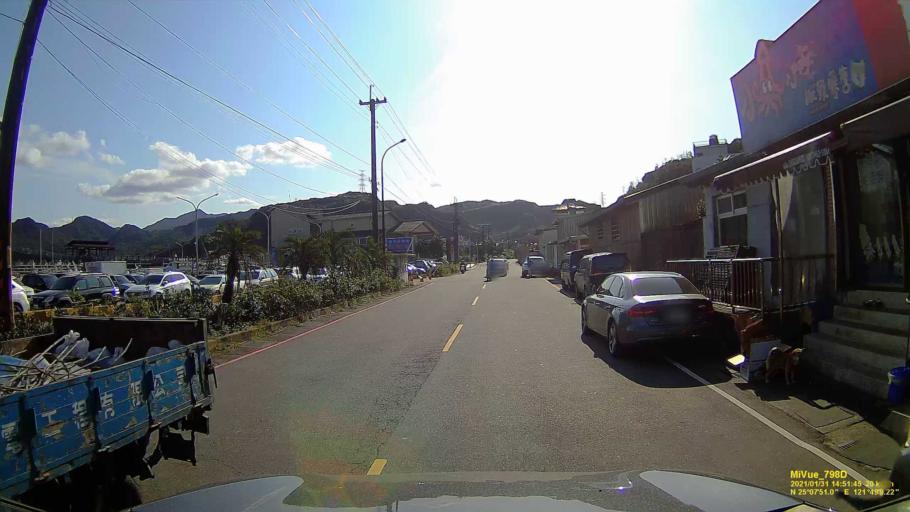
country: TW
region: Taiwan
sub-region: Keelung
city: Keelung
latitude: 25.1307
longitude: 121.8191
